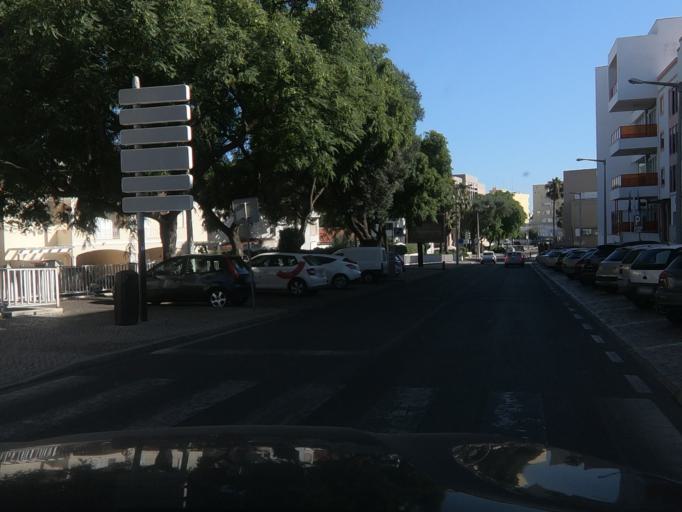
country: PT
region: Faro
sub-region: Loule
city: Loule
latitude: 37.1398
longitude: -8.0180
